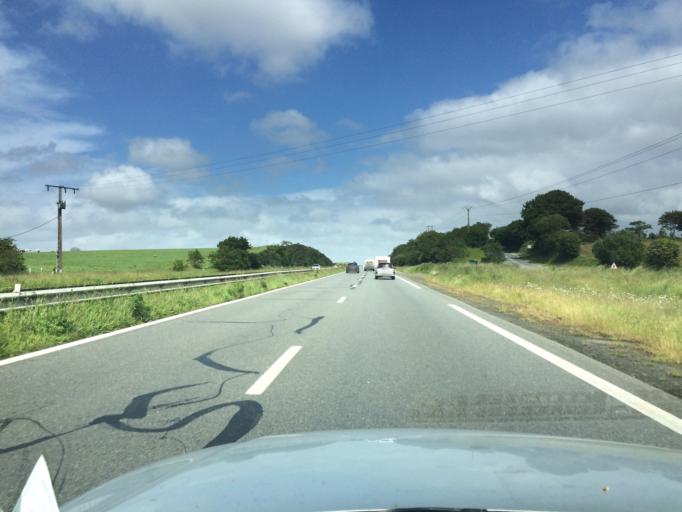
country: FR
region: Brittany
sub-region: Departement du Finistere
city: Guipavas
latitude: 48.4507
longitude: -4.3826
